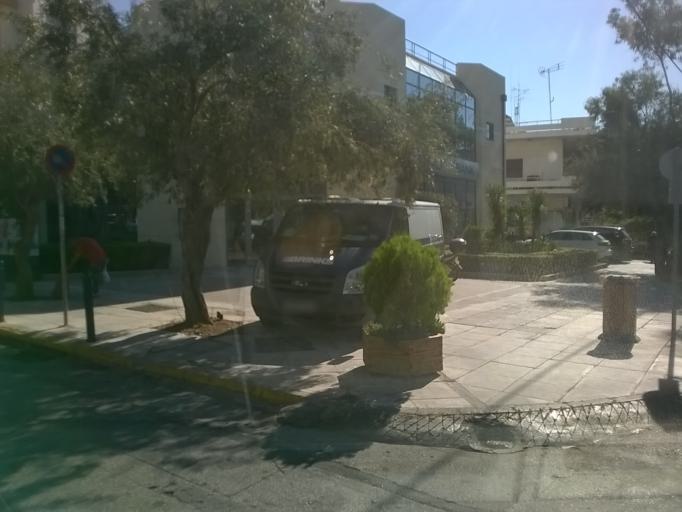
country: GR
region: Attica
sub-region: Nomarchia Anatolikis Attikis
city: Voula
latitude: 37.8395
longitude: 23.7673
